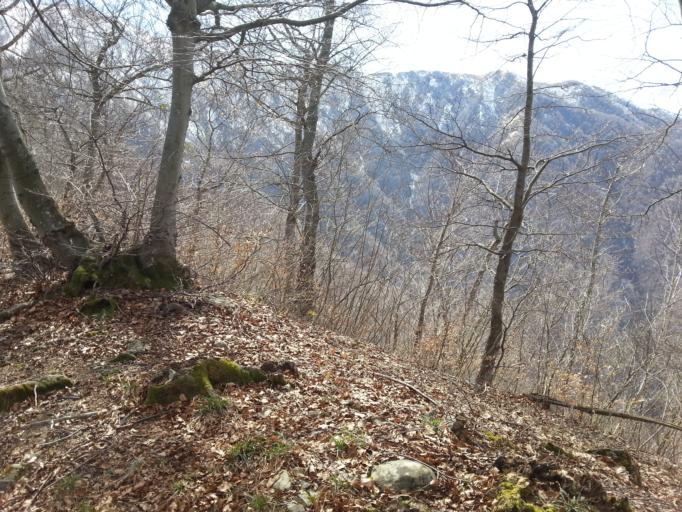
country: IT
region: Lombardy
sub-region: Provincia di Como
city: Lezzeno
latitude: 45.9294
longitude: 9.2193
